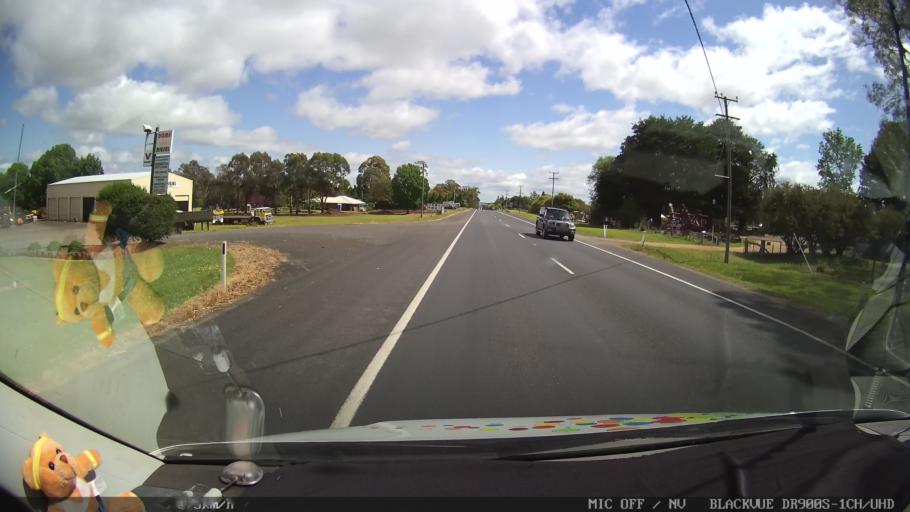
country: AU
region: New South Wales
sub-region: Glen Innes Severn
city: Glen Innes
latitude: -29.7657
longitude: 151.7330
